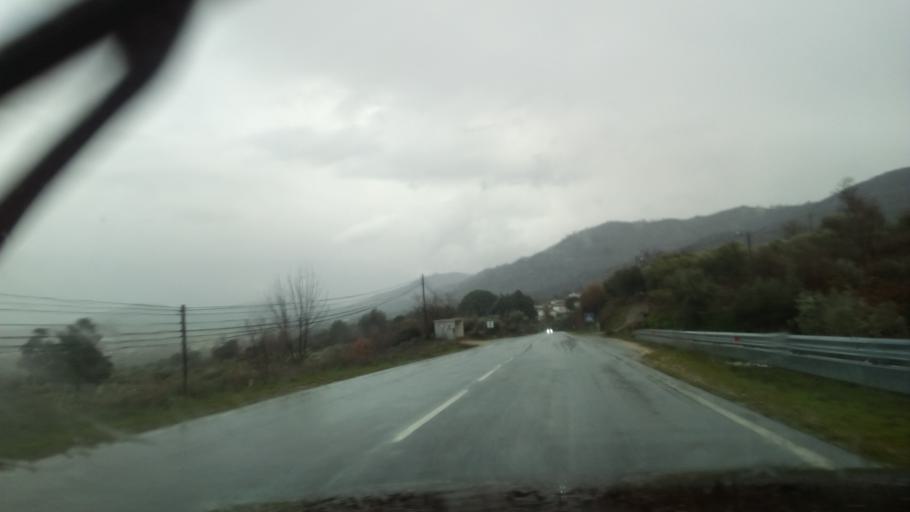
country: PT
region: Guarda
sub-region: Guarda
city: Guarda
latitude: 40.5836
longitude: -7.2926
